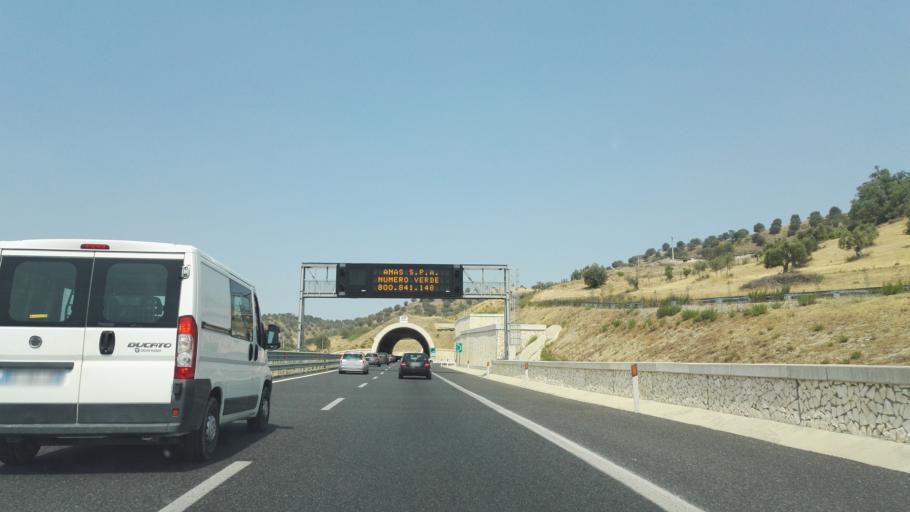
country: IT
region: Calabria
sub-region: Provincia di Cosenza
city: Tarsia
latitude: 39.5991
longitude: 16.2405
